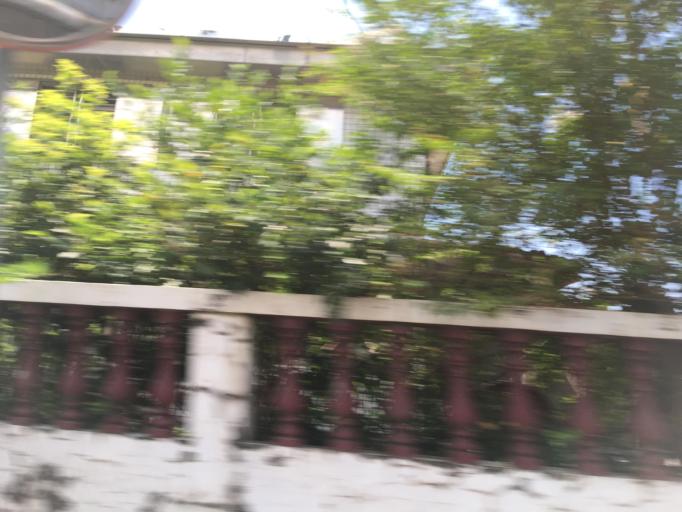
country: TW
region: Taiwan
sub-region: Yilan
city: Yilan
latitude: 24.6426
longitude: 121.7625
